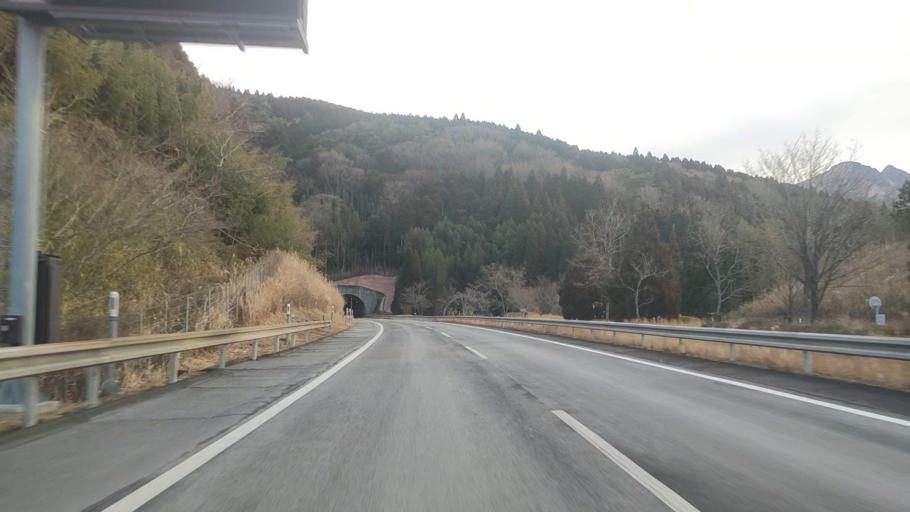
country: JP
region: Oita
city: Beppu
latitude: 33.2668
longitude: 131.3383
